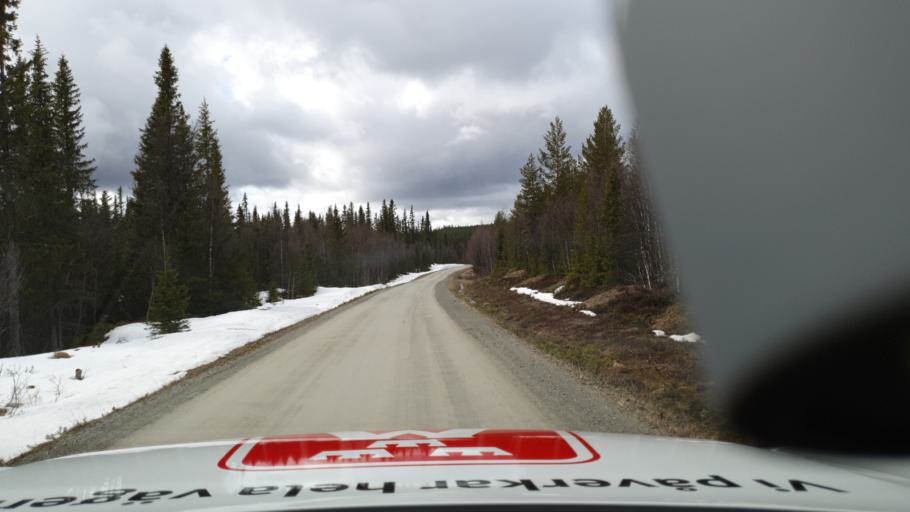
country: SE
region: Jaemtland
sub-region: Bergs Kommun
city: Hoverberg
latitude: 62.8432
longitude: 13.8379
